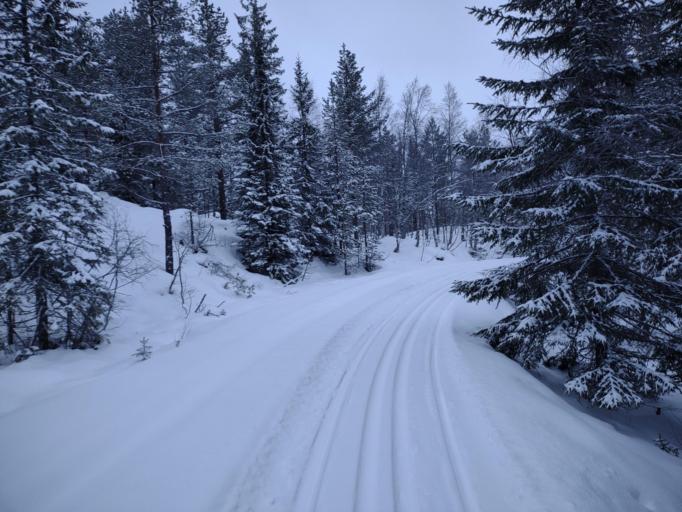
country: NO
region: Buskerud
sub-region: Flesberg
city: Lampeland
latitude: 59.7473
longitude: 9.4867
